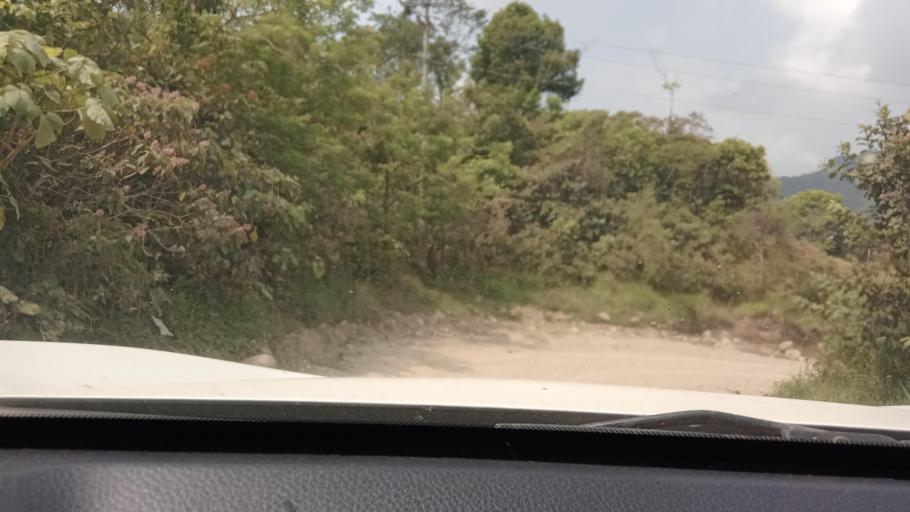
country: MX
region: Tabasco
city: Chontalpa
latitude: 17.4918
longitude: -93.6653
